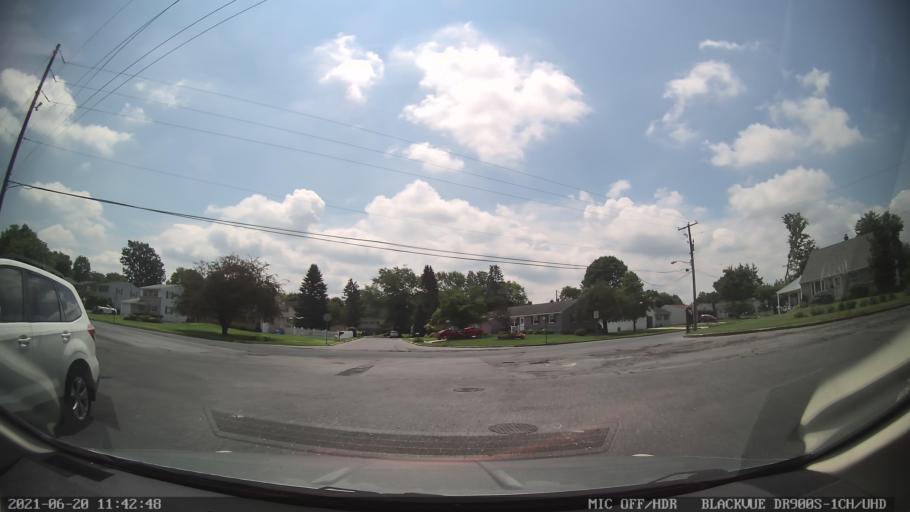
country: US
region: Pennsylvania
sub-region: Lehigh County
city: Dorneyville
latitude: 40.5830
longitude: -75.5102
